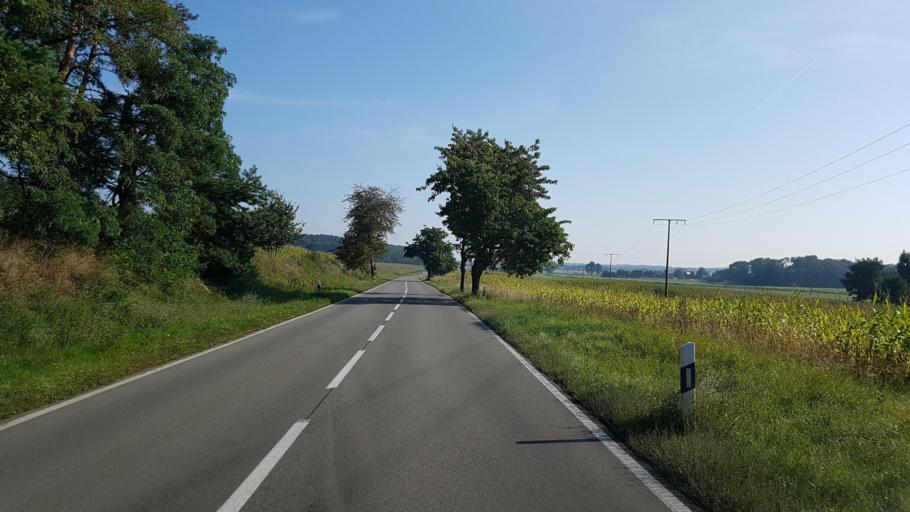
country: DE
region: Brandenburg
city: Pawesin
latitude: 52.4962
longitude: 12.6170
